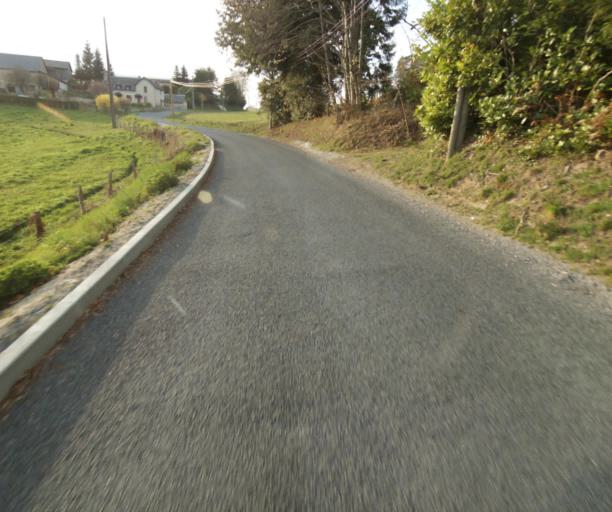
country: FR
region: Limousin
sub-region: Departement de la Correze
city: Correze
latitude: 45.3721
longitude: 1.8684
